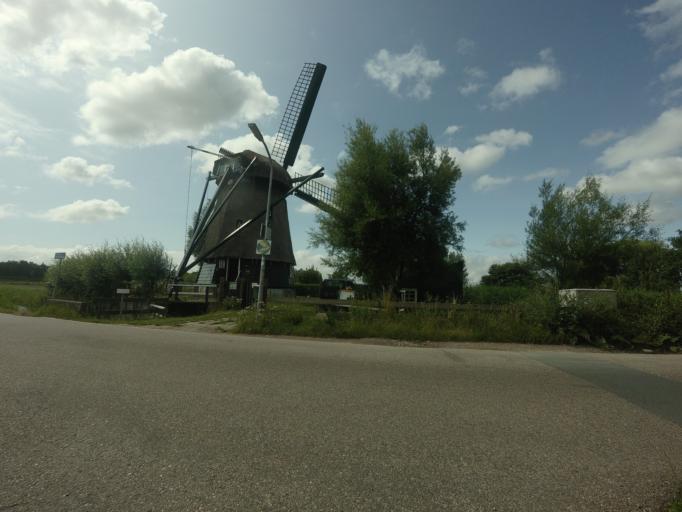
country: NL
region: North Holland
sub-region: Gemeente Haarlem
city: Haarlem
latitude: 52.3905
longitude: 4.6736
